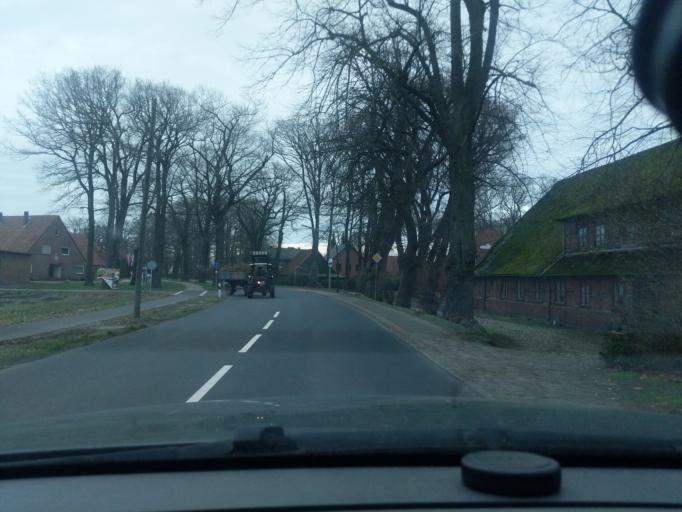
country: DE
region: Lower Saxony
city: Helvesiek
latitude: 53.2139
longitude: 9.4916
